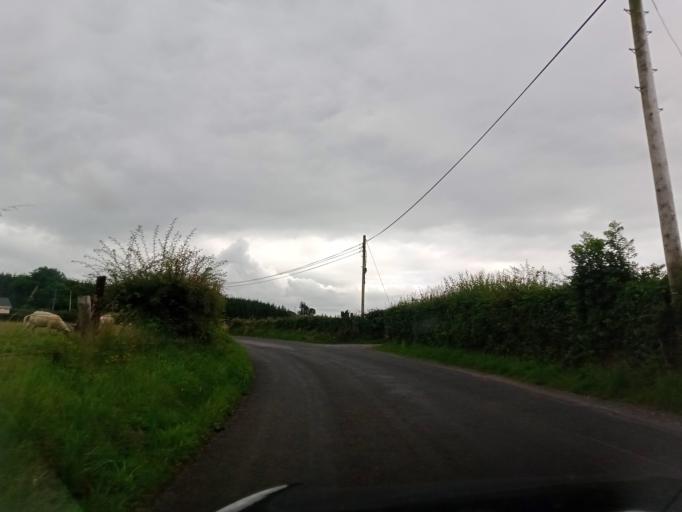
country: IE
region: Leinster
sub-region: Kilkenny
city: Castlecomer
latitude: 52.8953
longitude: -7.1439
